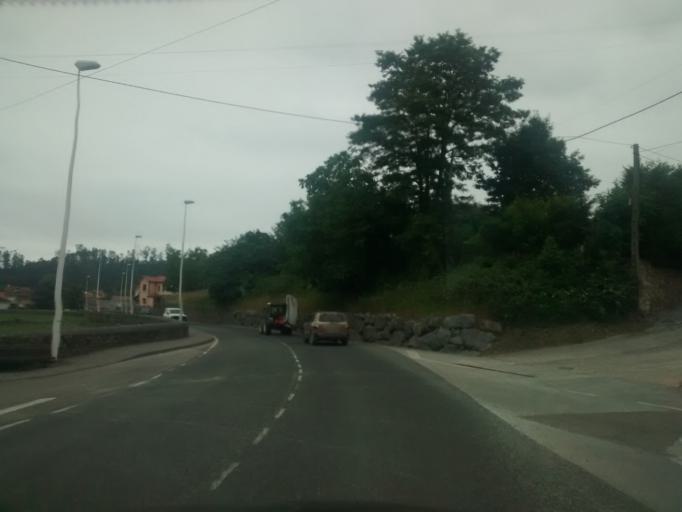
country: ES
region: Cantabria
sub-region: Provincia de Cantabria
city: Luzmela
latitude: 43.3147
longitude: -4.1934
